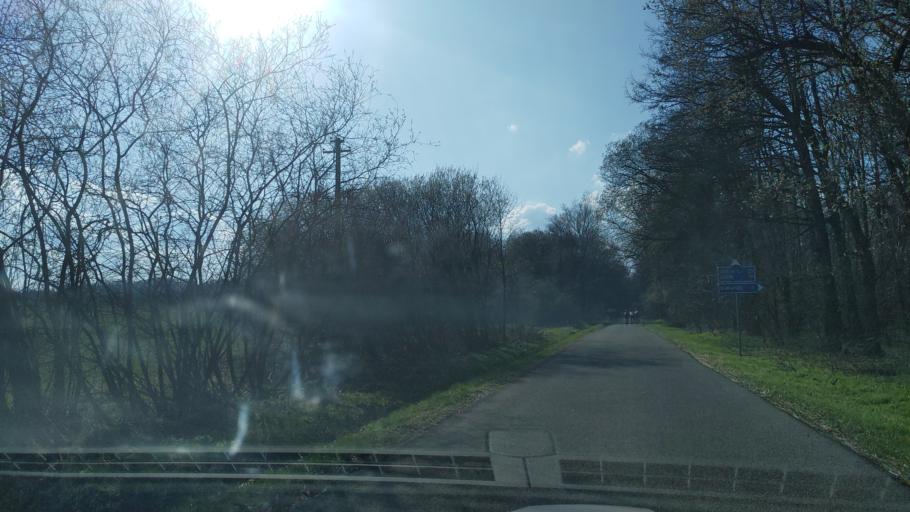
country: CZ
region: Ustecky
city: Vernerice
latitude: 50.6833
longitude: 14.2937
